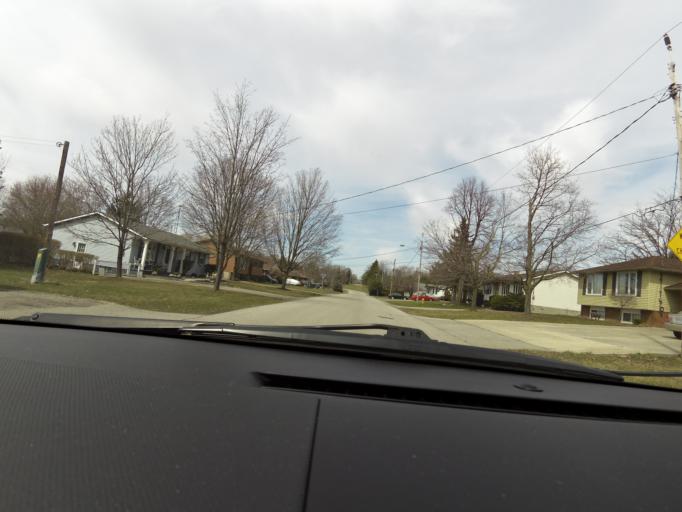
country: CA
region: Ontario
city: Ancaster
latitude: 42.9433
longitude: -79.8542
